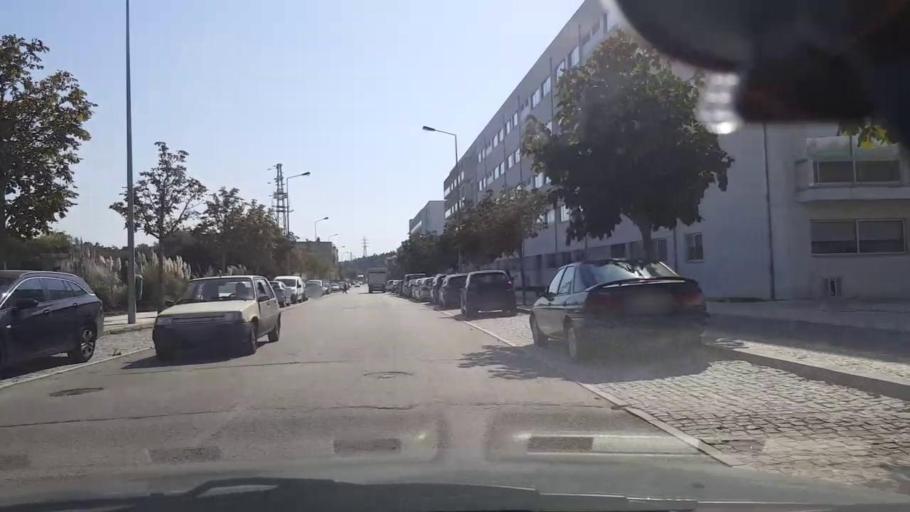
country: PT
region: Porto
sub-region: Vila do Conde
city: Vila do Conde
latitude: 41.3581
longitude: -8.7323
